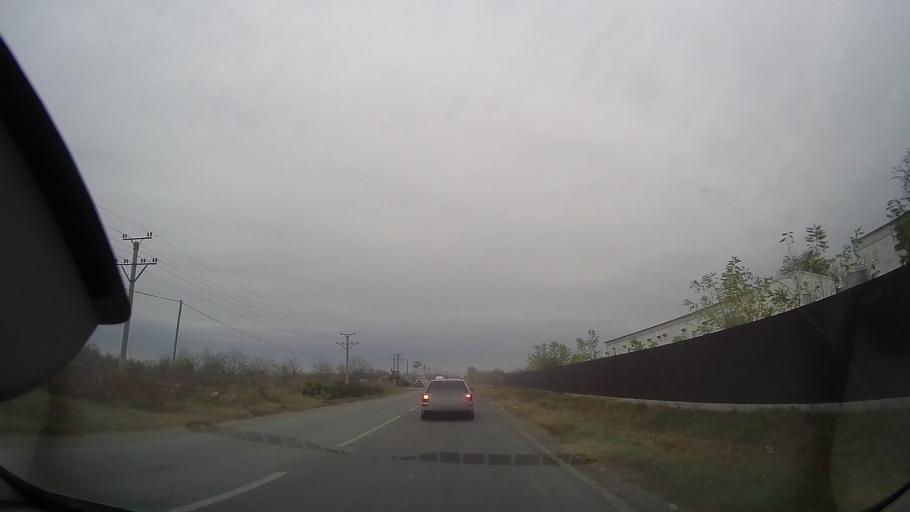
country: RO
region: Ialomita
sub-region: Oras Amara
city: Amara
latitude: 44.5896
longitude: 27.3307
